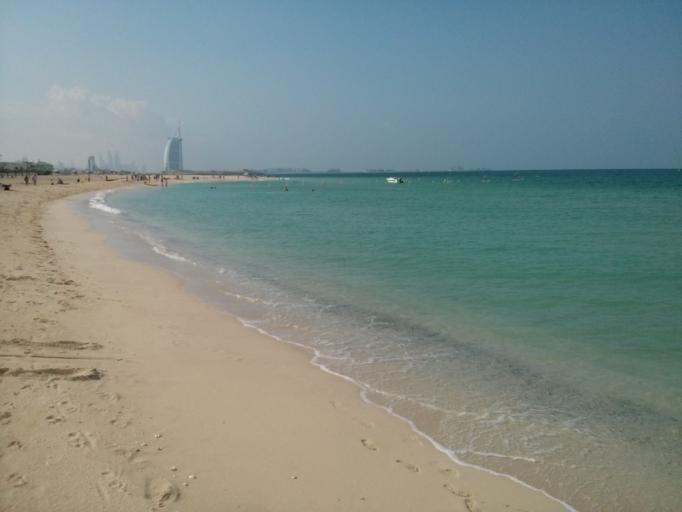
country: AE
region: Dubai
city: Dubai
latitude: 25.1668
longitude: 55.2094
